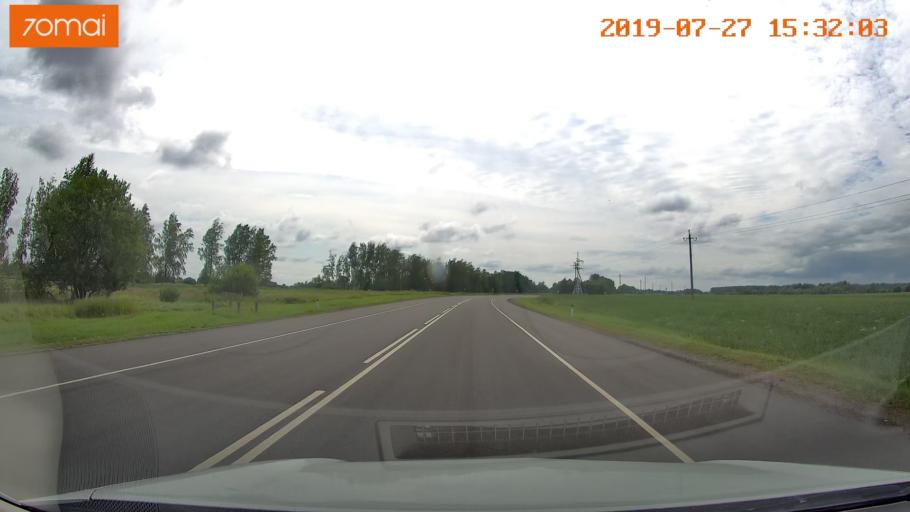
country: RU
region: Kaliningrad
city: Nesterov
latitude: 54.6179
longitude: 22.4796
